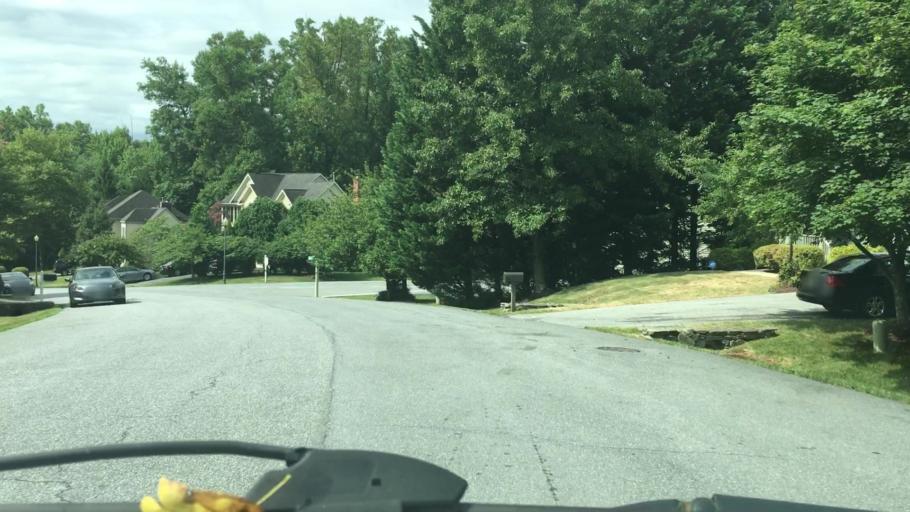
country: US
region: Maryland
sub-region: Prince George's County
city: Glenn Dale
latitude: 38.9924
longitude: -76.7842
